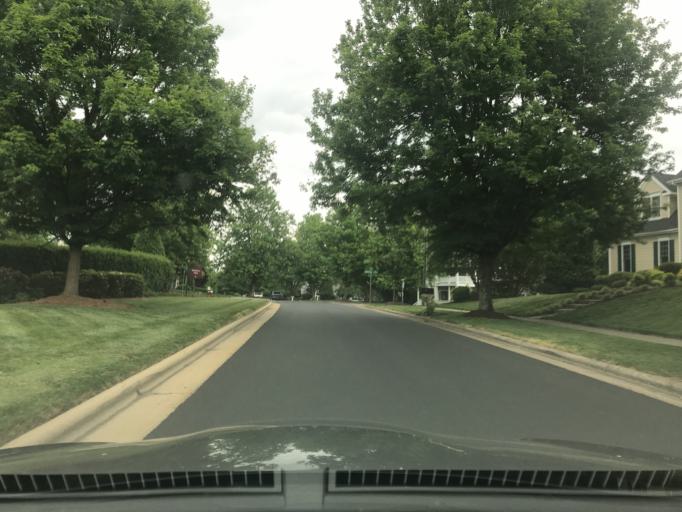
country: US
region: North Carolina
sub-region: Wake County
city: Wake Forest
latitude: 35.9127
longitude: -78.5830
